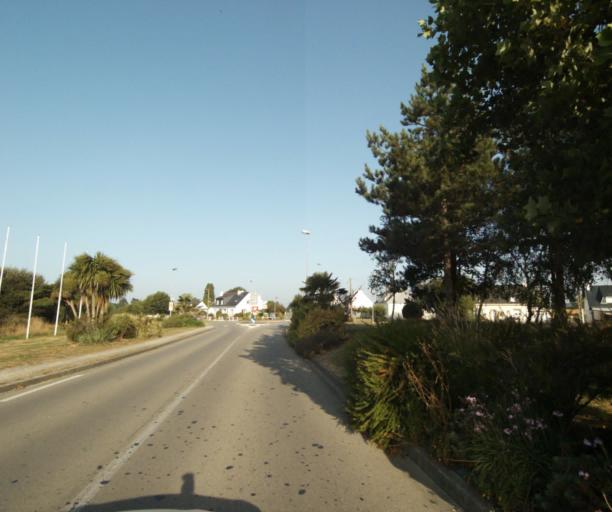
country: FR
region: Brittany
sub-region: Departement du Morbihan
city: Riantec
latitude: 47.7111
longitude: -3.2988
